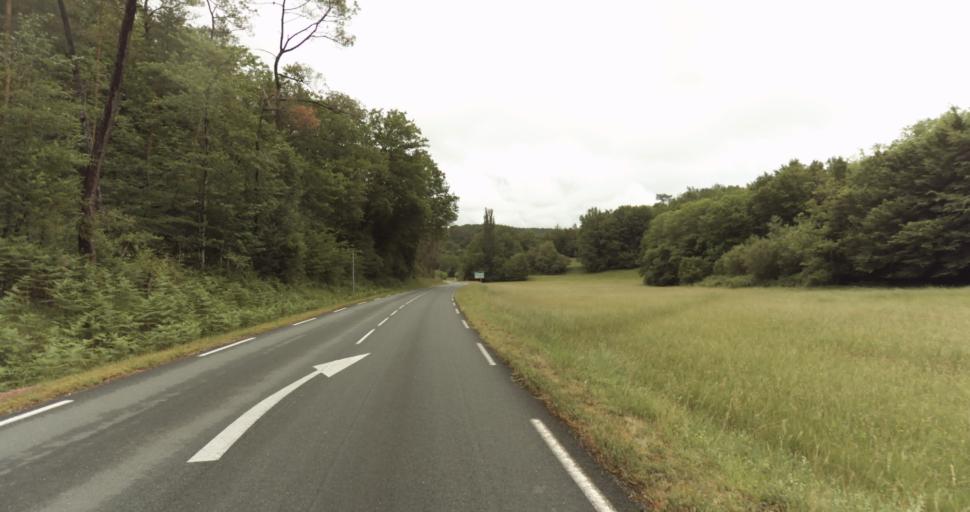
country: FR
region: Aquitaine
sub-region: Departement de la Dordogne
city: Belves
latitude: 44.6660
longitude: 1.0128
